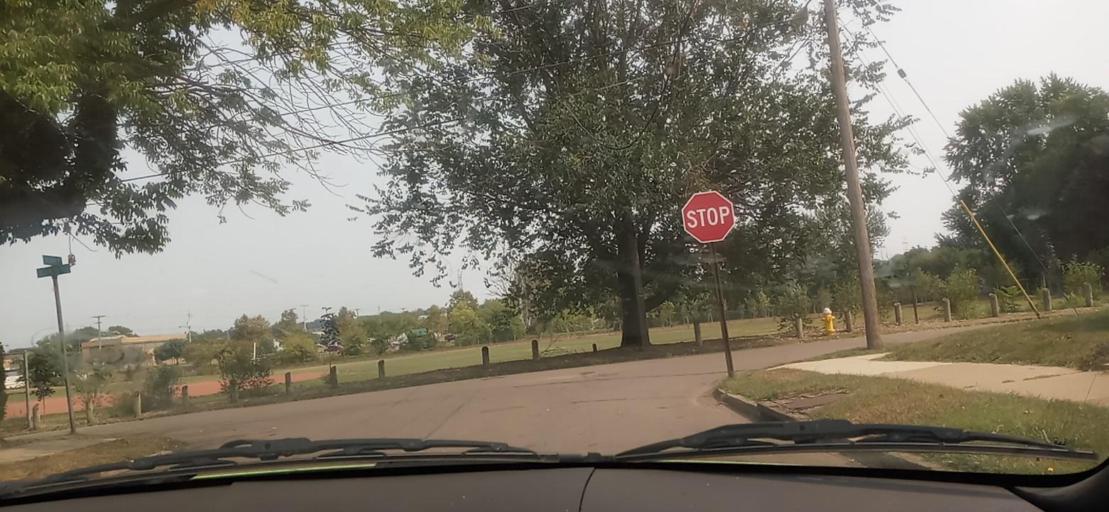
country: US
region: Ohio
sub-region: Summit County
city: Portage Lakes
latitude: 41.0388
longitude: -81.5425
